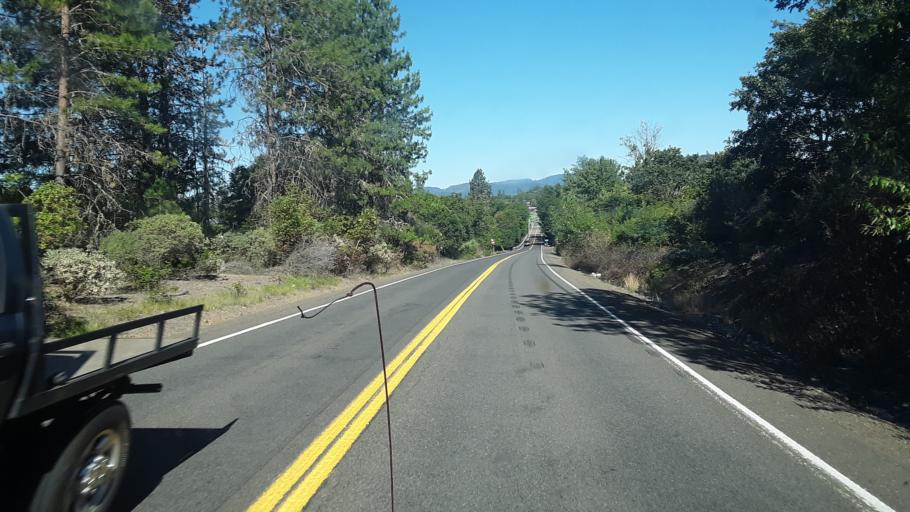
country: US
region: Oregon
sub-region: Jackson County
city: Eagle Point
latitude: 42.5240
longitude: -122.8366
